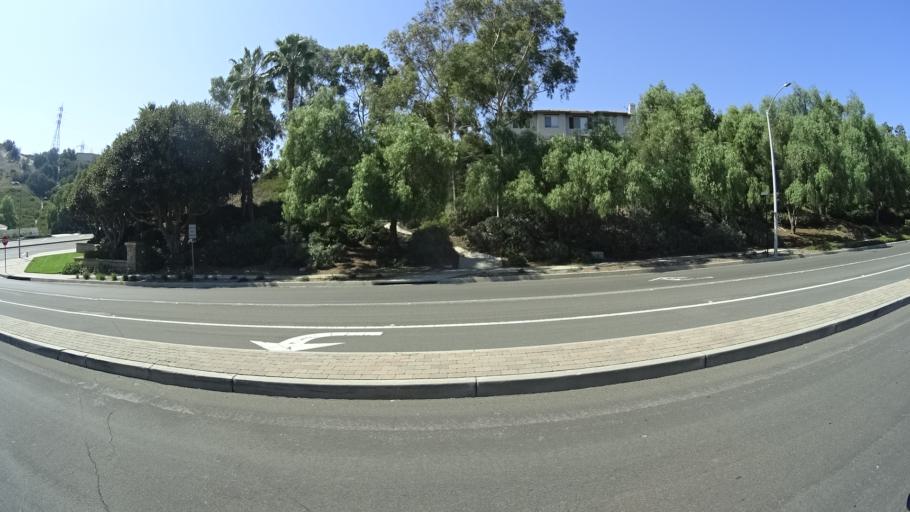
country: US
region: California
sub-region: Orange County
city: San Clemente
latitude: 33.4566
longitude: -117.5760
